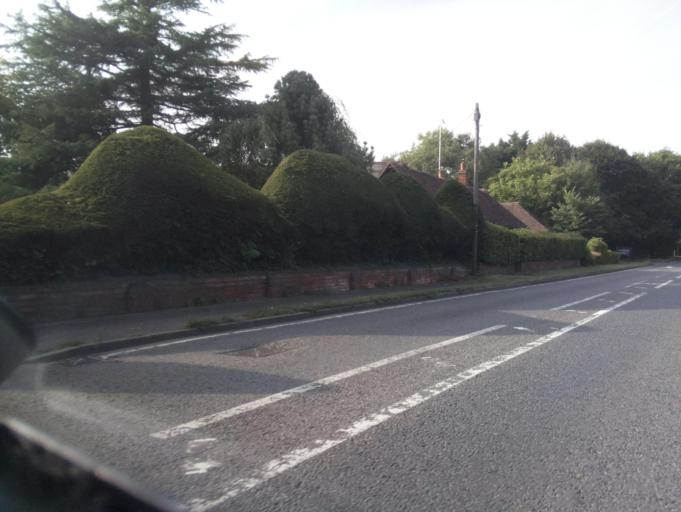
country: GB
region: England
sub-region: Warwickshire
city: Studley
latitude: 52.2436
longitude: -1.8846
